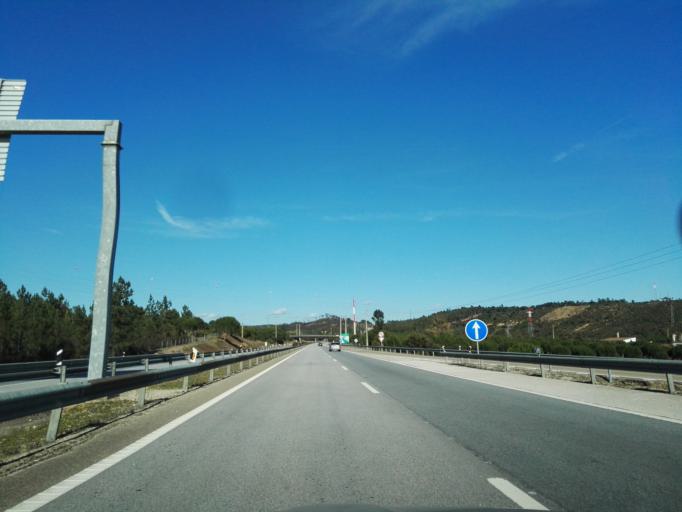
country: PT
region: Santarem
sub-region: Abrantes
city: Abrantes
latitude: 39.4814
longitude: -8.2244
